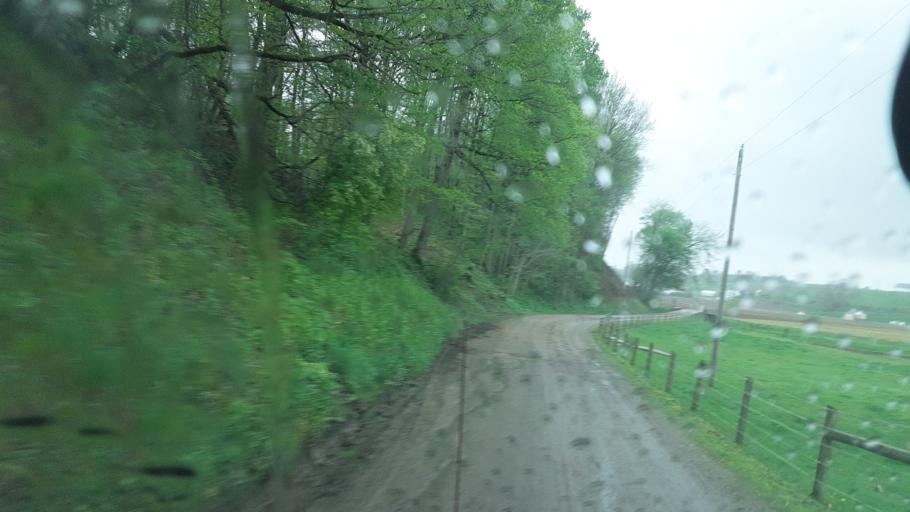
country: US
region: Ohio
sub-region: Holmes County
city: Millersburg
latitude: 40.4765
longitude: -81.8262
